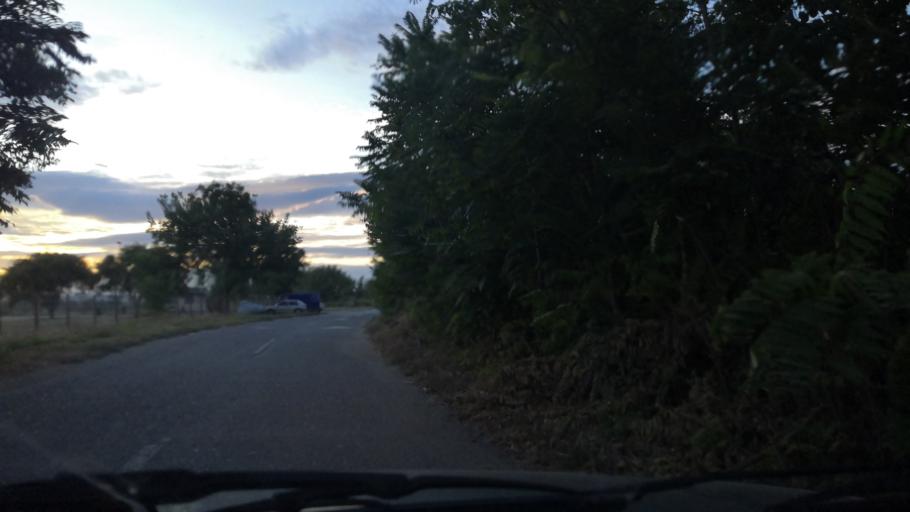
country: RO
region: Mehedinti
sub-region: Comuna Gruia
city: Izvoarele
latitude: 44.2876
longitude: 22.6204
